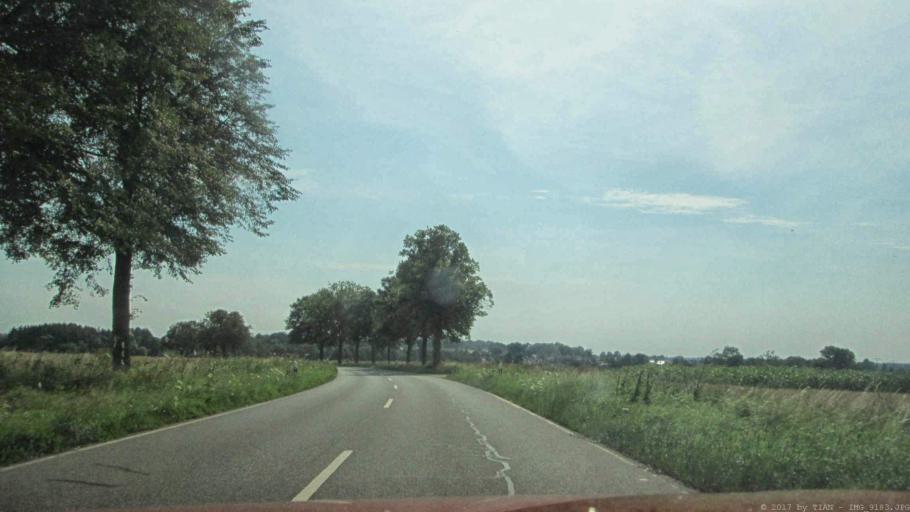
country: DE
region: Lower Saxony
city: Wolfsburg
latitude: 52.4068
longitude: 10.8438
